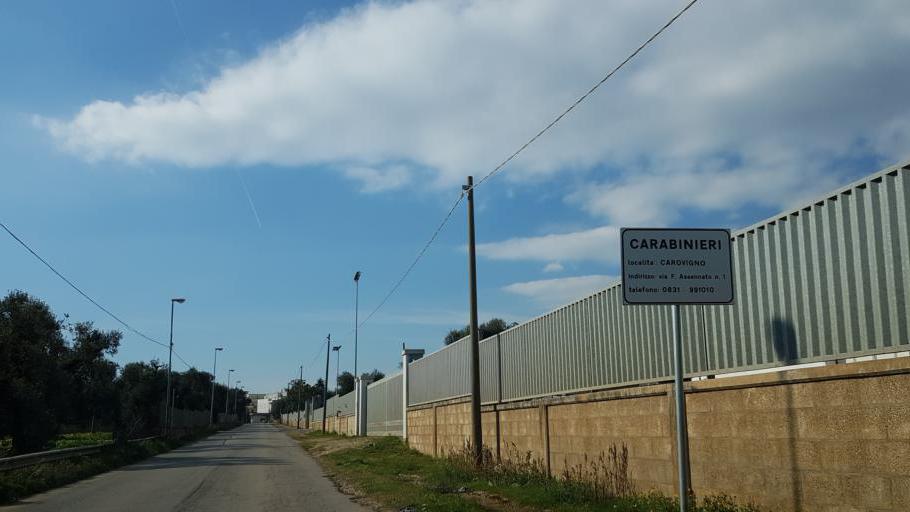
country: IT
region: Apulia
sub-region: Provincia di Brindisi
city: Carovigno
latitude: 40.7115
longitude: 17.6686
